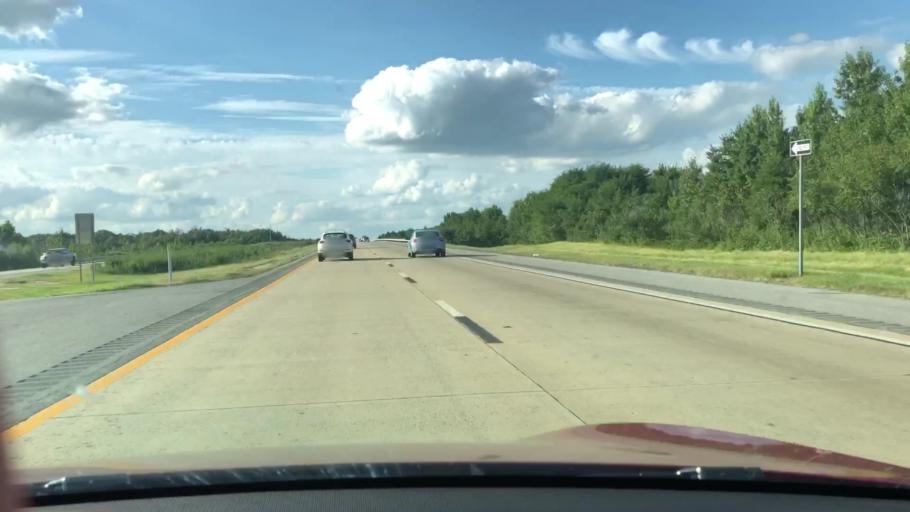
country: US
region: Delaware
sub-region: New Castle County
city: Townsend
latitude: 39.3815
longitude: -75.6613
